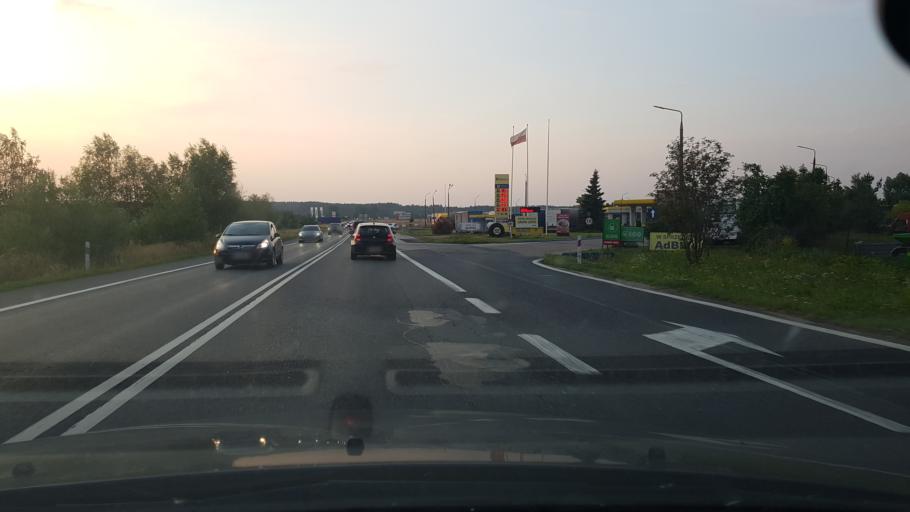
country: PL
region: Masovian Voivodeship
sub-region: Powiat mlawski
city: Mlawa
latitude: 53.1161
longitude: 20.3982
